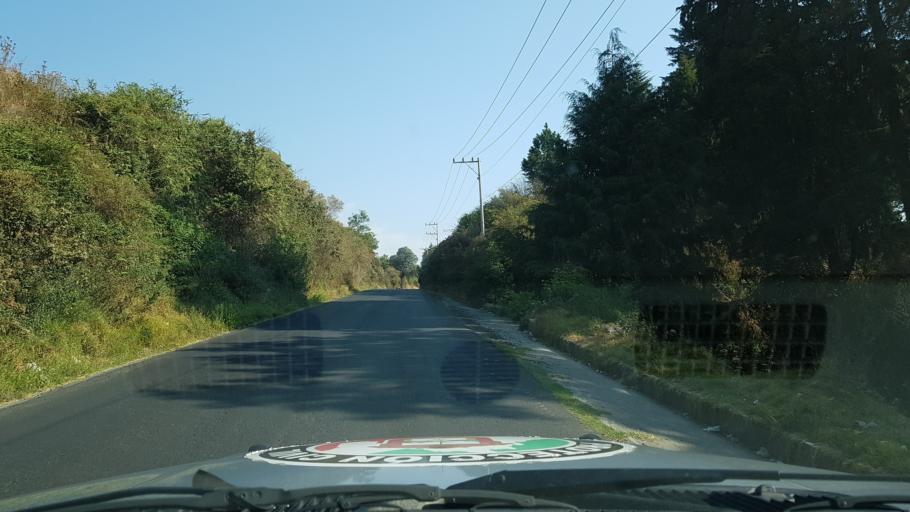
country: MX
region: Mexico
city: Atlautla
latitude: 19.0399
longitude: -98.7739
